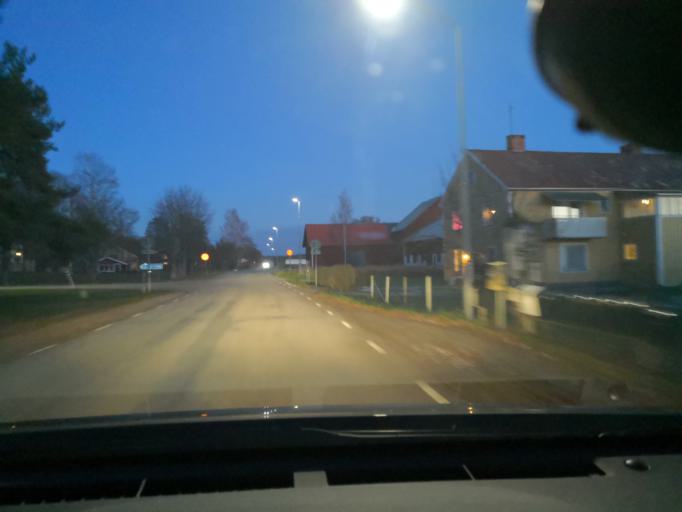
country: SE
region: Vaestmanland
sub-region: Sala Kommun
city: Sala
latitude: 59.8700
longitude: 16.7205
